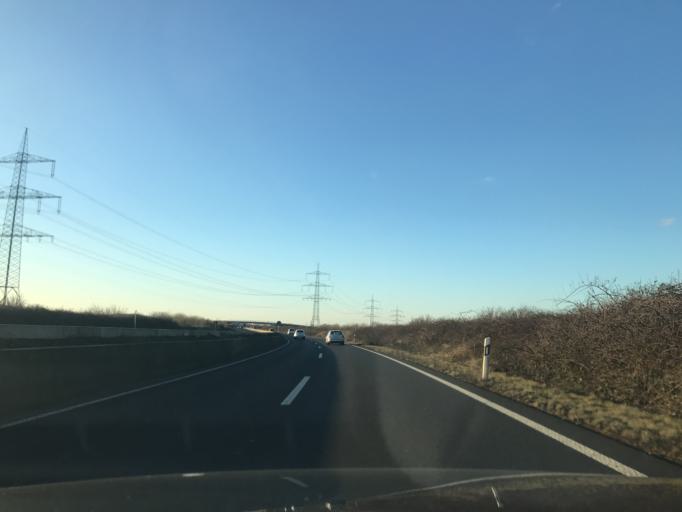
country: DE
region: North Rhine-Westphalia
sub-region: Regierungsbezirk Dusseldorf
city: Ratingen
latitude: 51.3216
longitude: 6.7613
